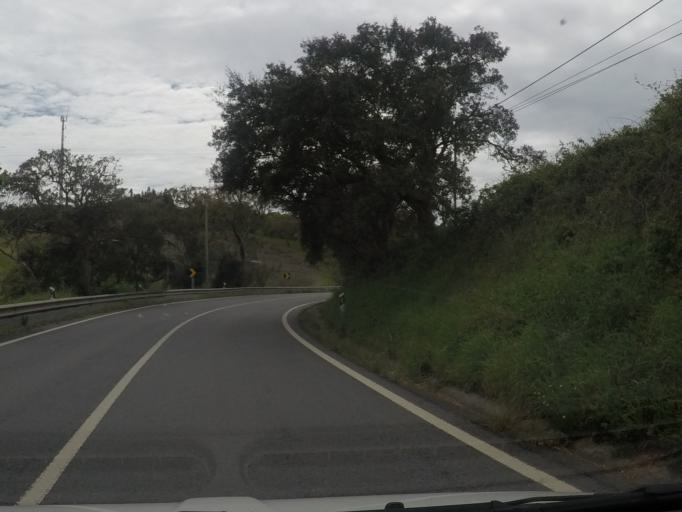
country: PT
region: Setubal
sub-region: Sines
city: Porto Covo
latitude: 37.8660
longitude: -8.7282
